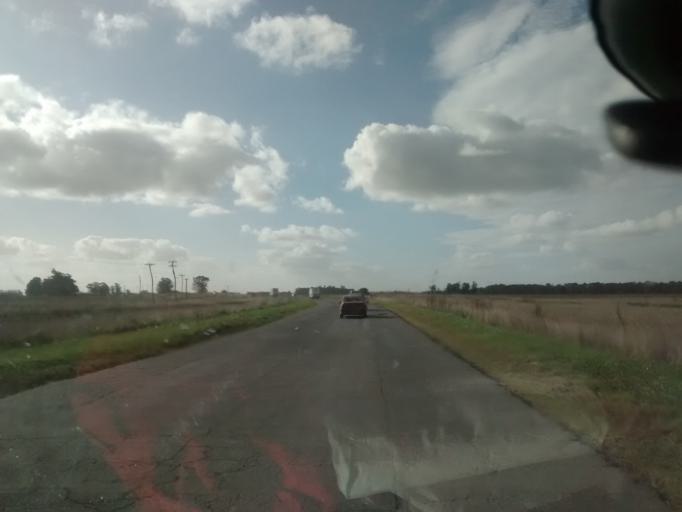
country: AR
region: Buenos Aires
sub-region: Partido de Ayacucho
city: Ayacucho
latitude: -37.1814
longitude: -58.5142
